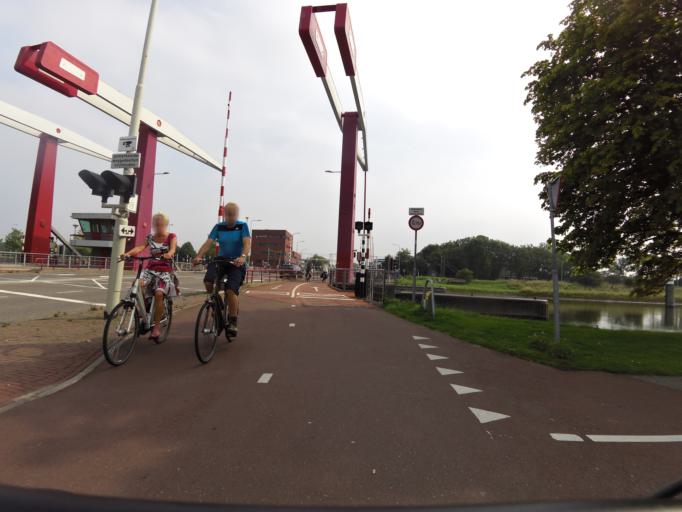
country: NL
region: Zeeland
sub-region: Gemeente Middelburg
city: Middelburg
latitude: 51.4945
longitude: 3.6128
